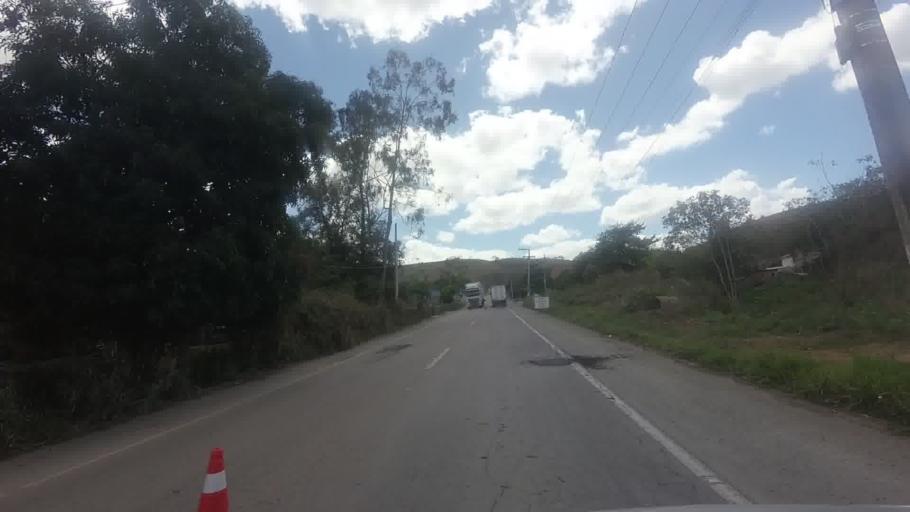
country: BR
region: Rio de Janeiro
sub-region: Santo Antonio De Padua
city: Santo Antonio de Padua
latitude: -21.6278
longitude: -42.2619
